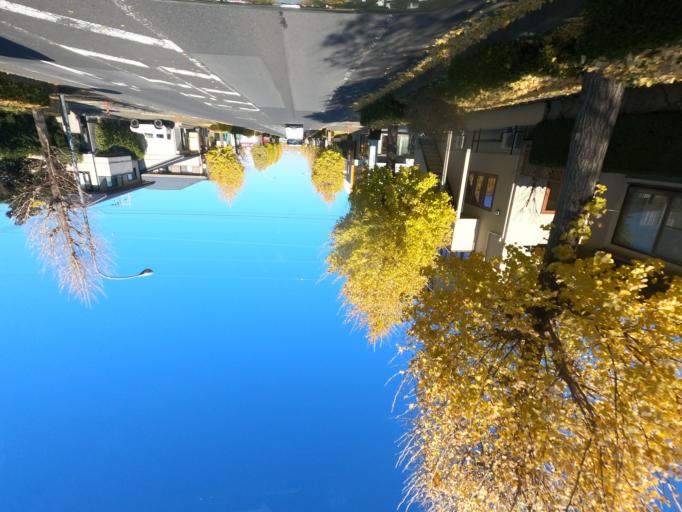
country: JP
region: Ibaraki
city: Mitsukaido
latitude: 35.9722
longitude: 139.9709
